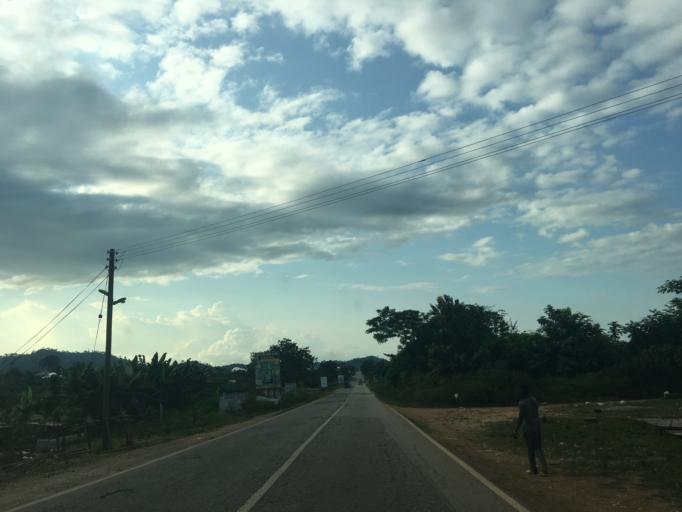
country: GH
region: Western
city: Bibiani
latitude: 6.4221
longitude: -2.3044
